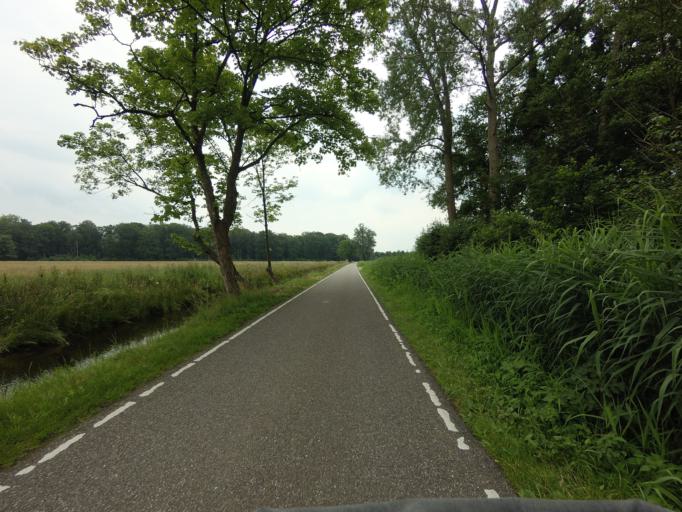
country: NL
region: Utrecht
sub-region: Gemeente Utrechtse Heuvelrug
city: Doorn
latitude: 52.0267
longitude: 5.3153
